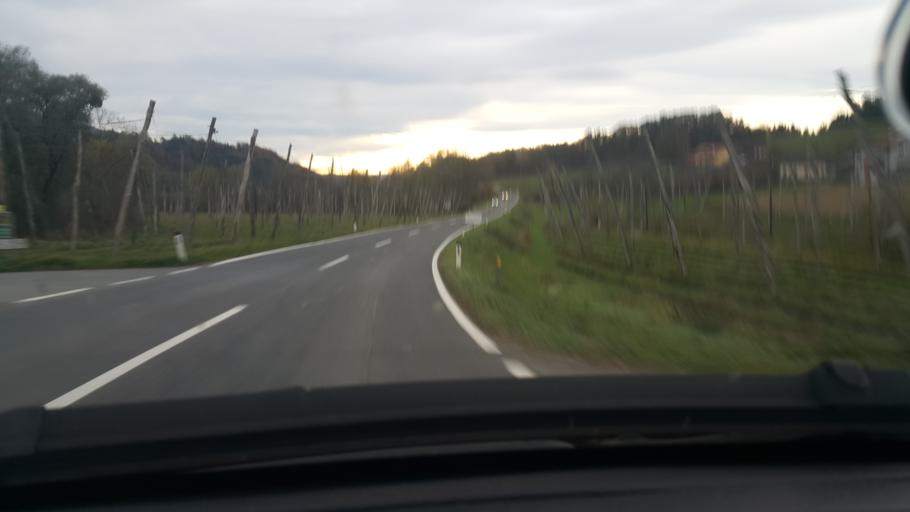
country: AT
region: Styria
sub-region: Politischer Bezirk Leibnitz
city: Leutschach
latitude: 46.6677
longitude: 15.4554
